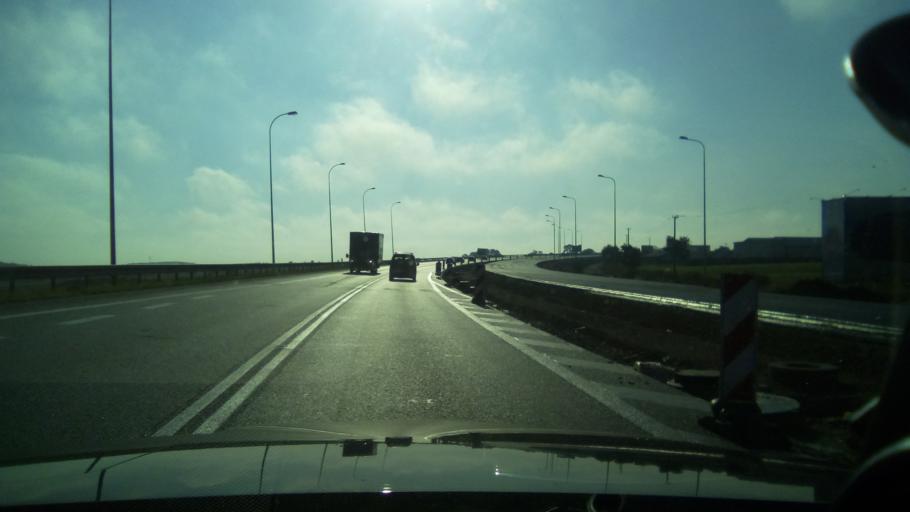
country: PL
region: Silesian Voivodeship
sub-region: Powiat bedzinski
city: Mierzecice
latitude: 50.4503
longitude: 19.1303
